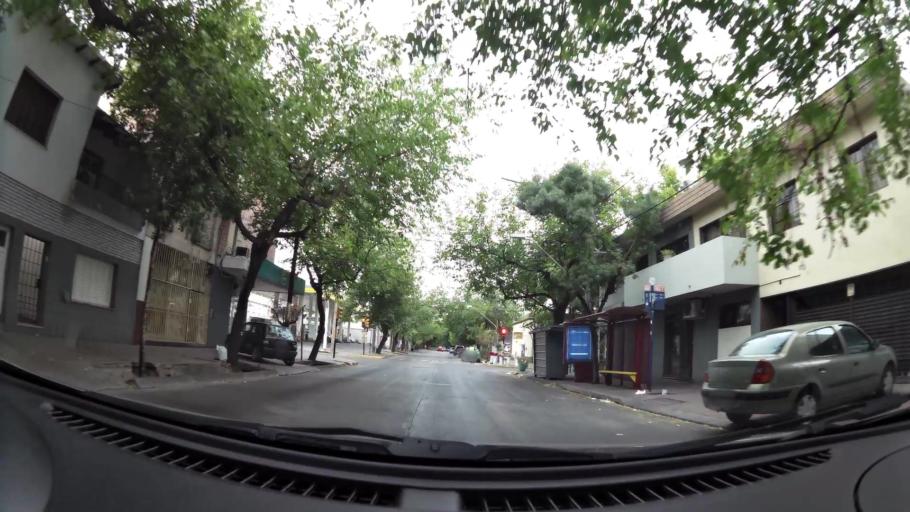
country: AR
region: Mendoza
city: Mendoza
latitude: -32.8777
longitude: -68.8566
